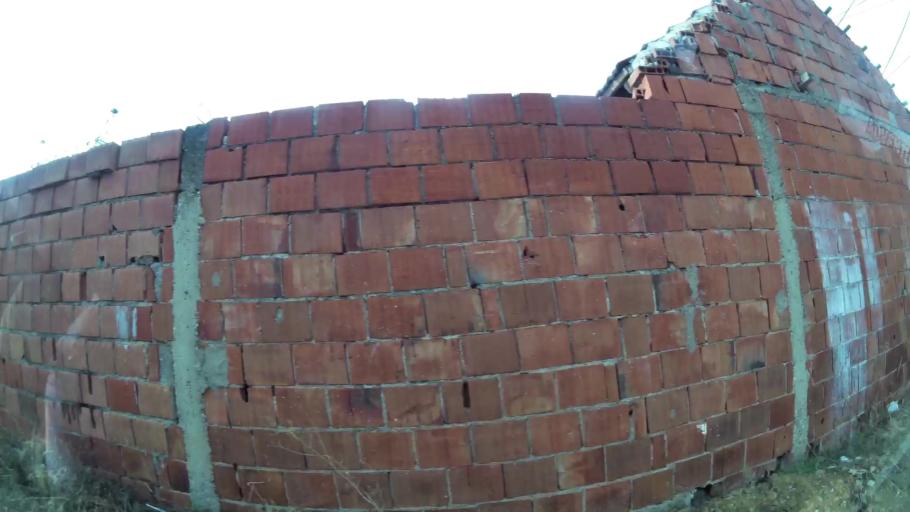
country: XK
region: Pristina
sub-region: Komuna e Prishtines
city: Pristina
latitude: 42.6926
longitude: 21.1696
